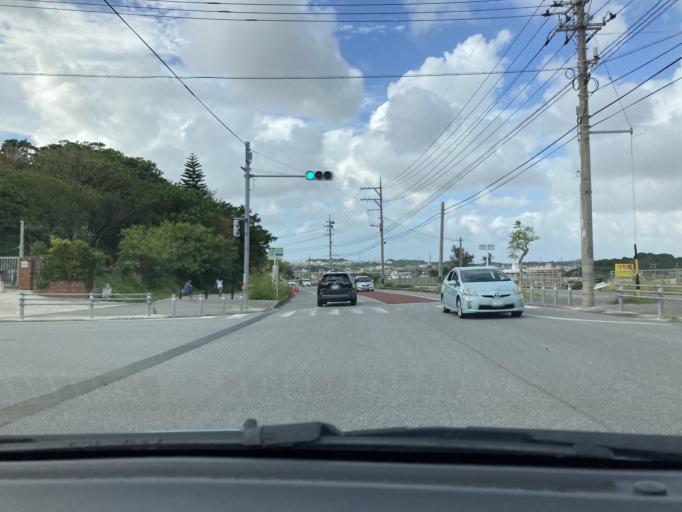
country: JP
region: Okinawa
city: Itoman
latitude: 26.1270
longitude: 127.6911
